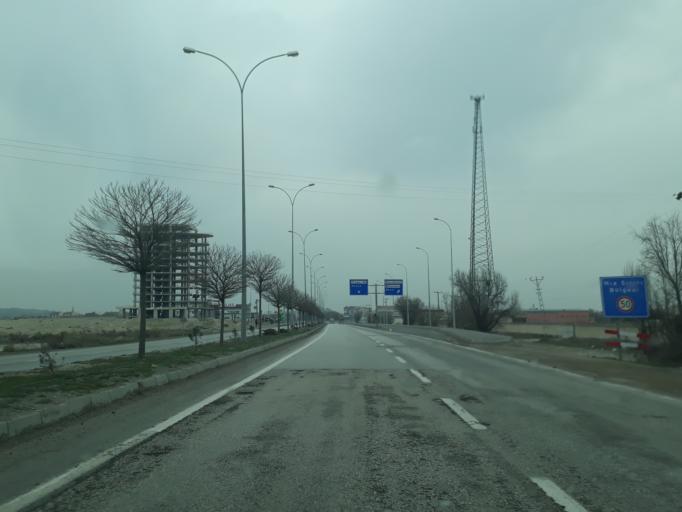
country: TR
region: Konya
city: Karapinar
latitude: 37.7153
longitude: 33.5732
